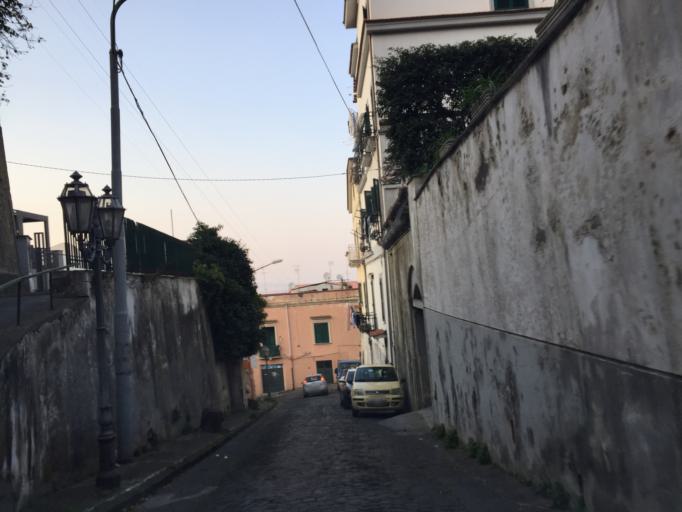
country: IT
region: Campania
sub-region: Provincia di Napoli
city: Castellammare di Stabia
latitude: 40.6886
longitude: 14.4820
